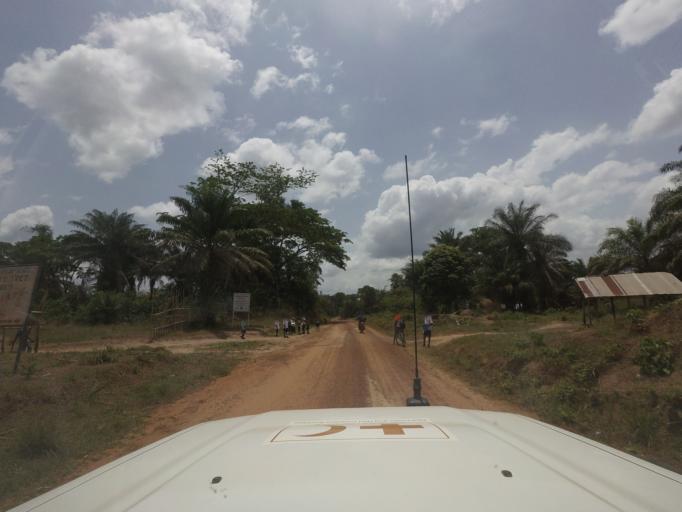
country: LR
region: Bong
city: Gbarnga
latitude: 7.1626
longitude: -9.2106
